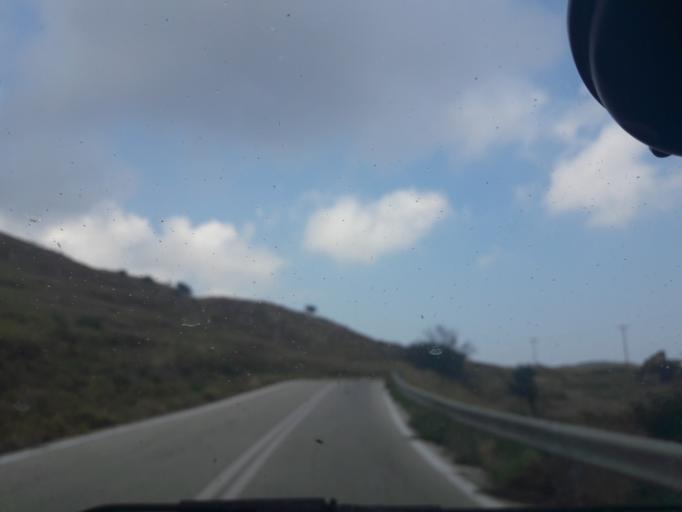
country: GR
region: North Aegean
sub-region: Nomos Lesvou
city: Myrina
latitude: 39.9567
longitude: 25.1656
